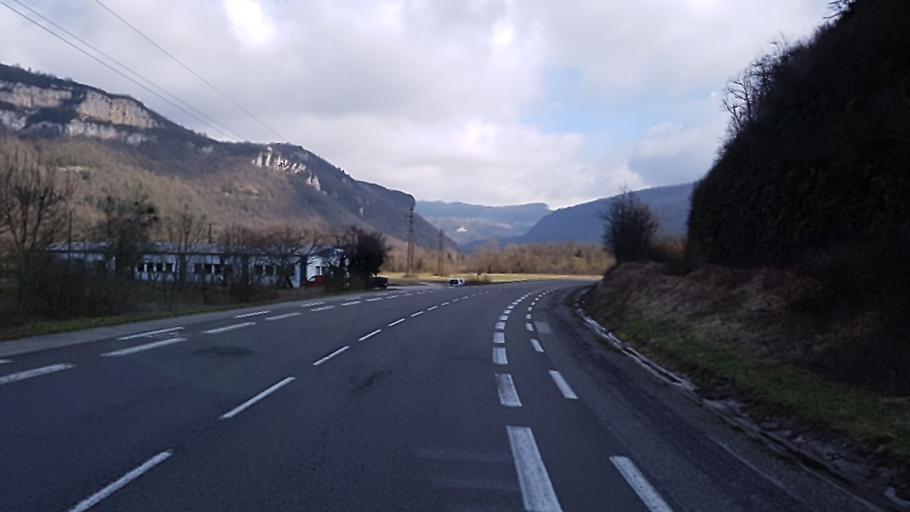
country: FR
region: Franche-Comte
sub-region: Departement du Jura
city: Lavans-les-Saint-Claude
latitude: 46.3669
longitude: 5.7272
